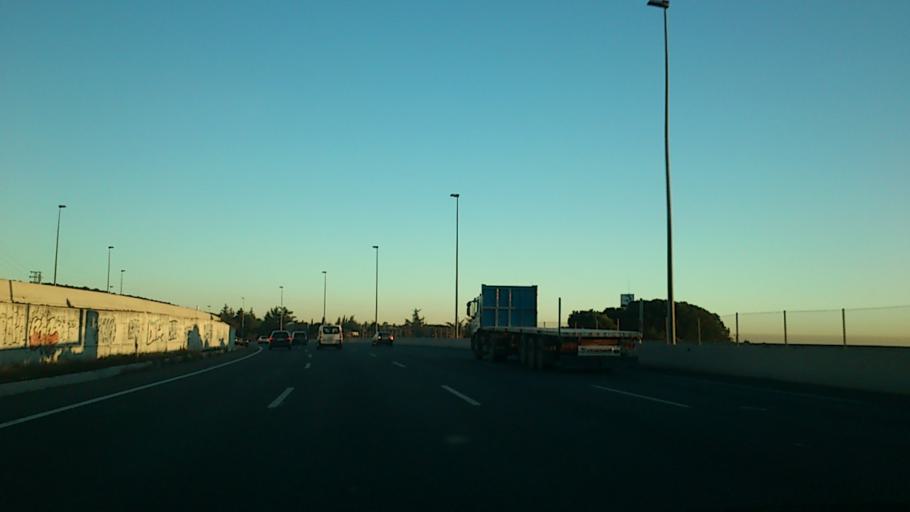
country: ES
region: Madrid
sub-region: Provincia de Madrid
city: Collado-Villalba
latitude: 40.6073
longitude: -3.9727
